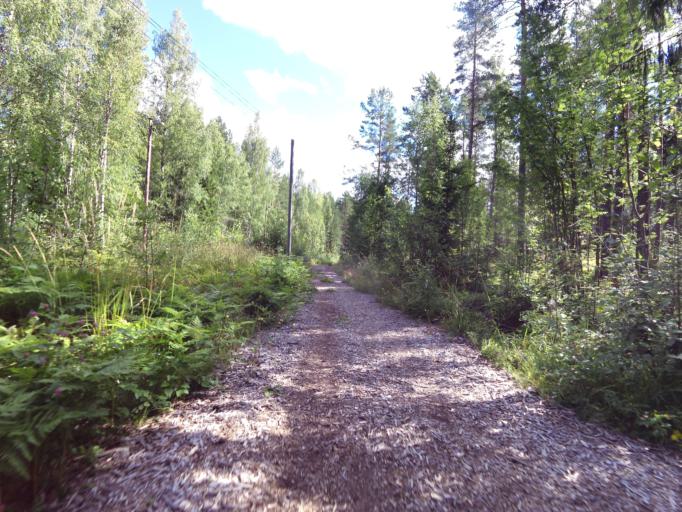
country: SE
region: Gaevleborg
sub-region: Hofors Kommun
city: Hofors
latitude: 60.5450
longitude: 16.2535
